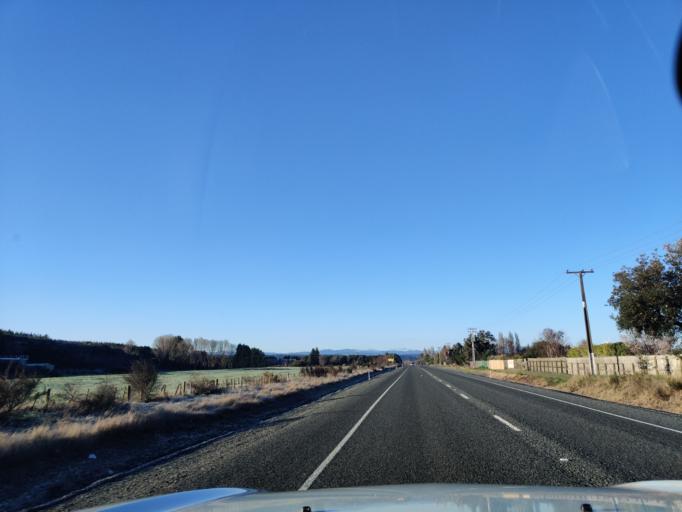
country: NZ
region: Waikato
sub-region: Taupo District
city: Taupo
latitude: -38.7528
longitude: 176.0744
